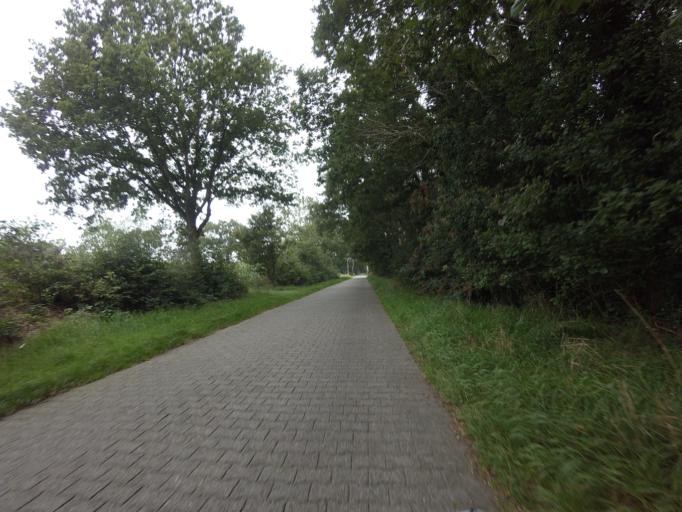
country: NL
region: Overijssel
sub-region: Gemeente Steenwijkerland
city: Steenwijkerwold
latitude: 52.8165
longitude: 6.0368
